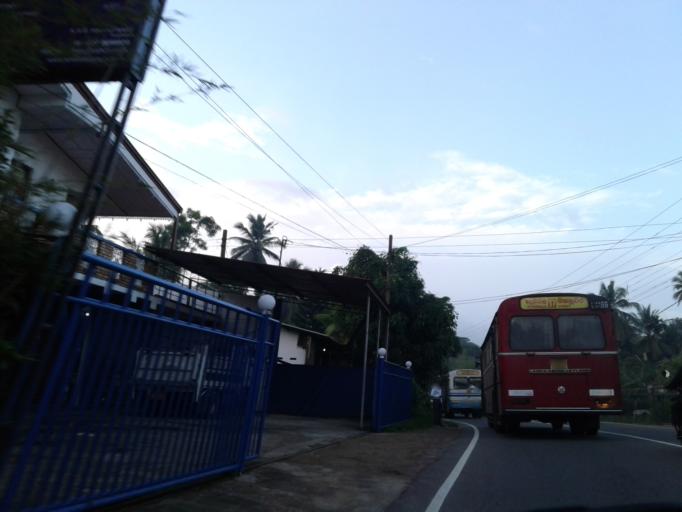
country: LK
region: Western
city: Gampaha
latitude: 7.0122
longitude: 80.0244
